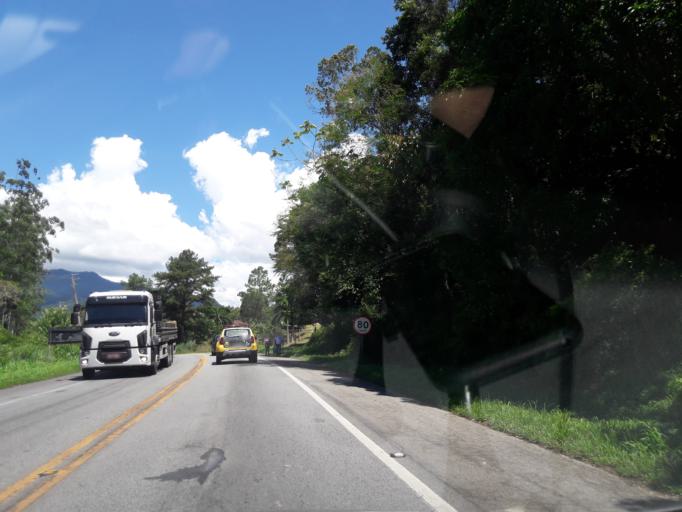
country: BR
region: Parana
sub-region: Antonina
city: Antonina
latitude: -25.5251
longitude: -48.7960
